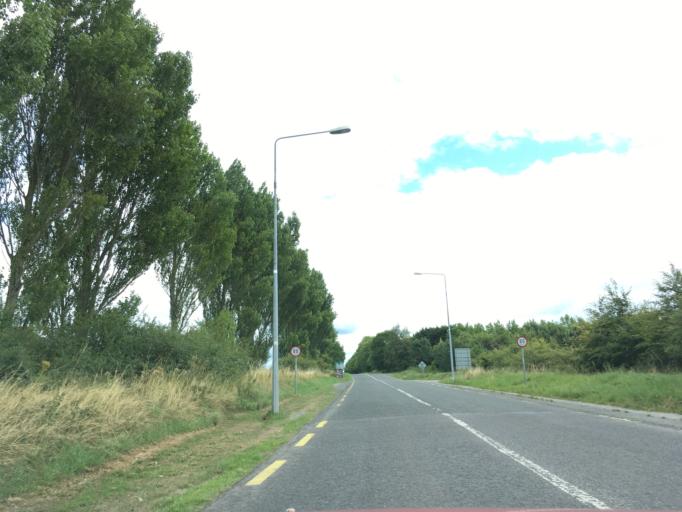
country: IE
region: Munster
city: Cashel
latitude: 52.5126
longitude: -7.9119
